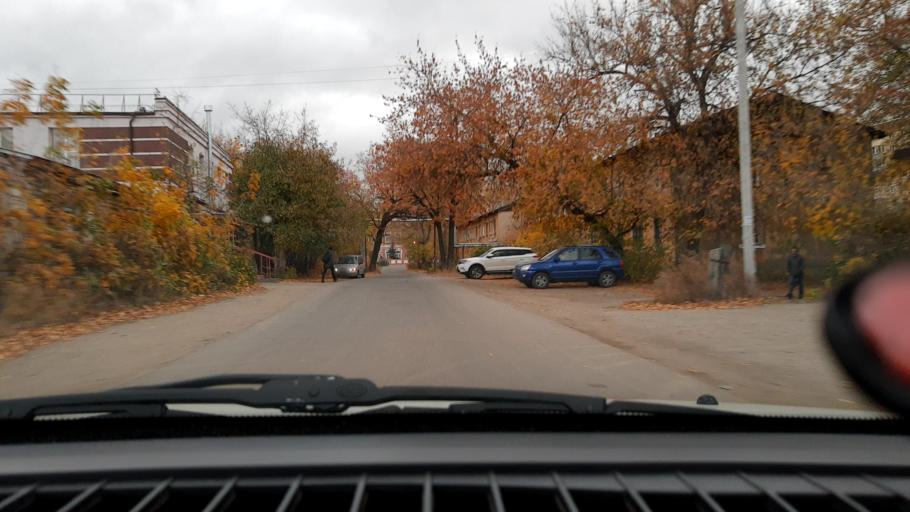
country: RU
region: Nizjnij Novgorod
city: Nizhniy Novgorod
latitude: 56.2940
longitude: 43.9493
